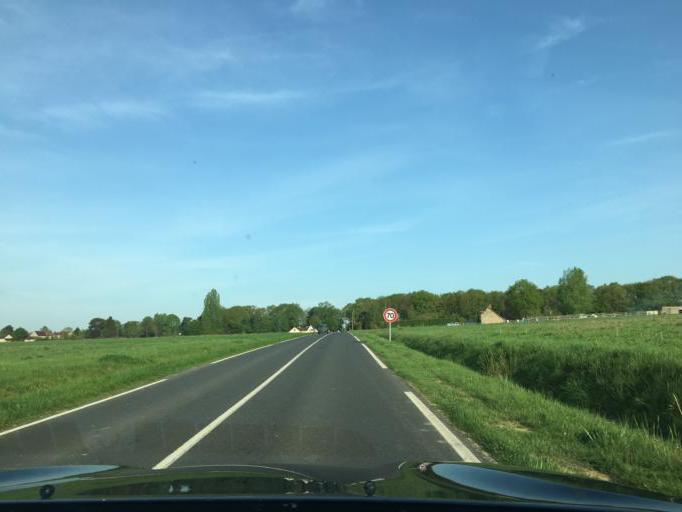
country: FR
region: Centre
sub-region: Departement d'Eure-et-Loir
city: Epernon
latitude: 48.6525
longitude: 1.6840
